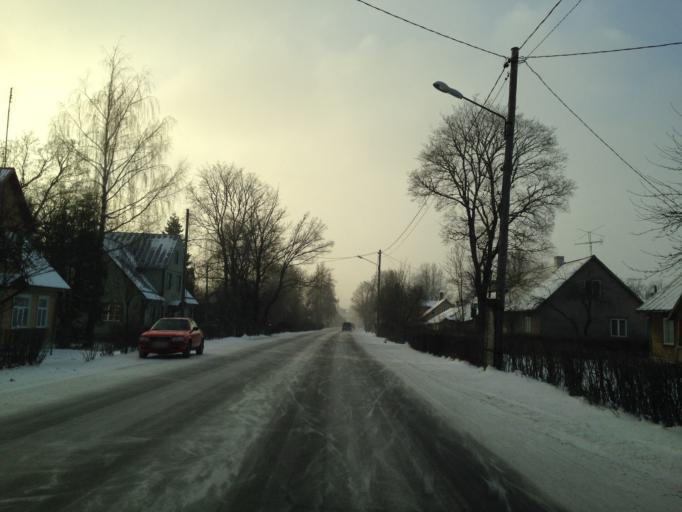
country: EE
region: Raplamaa
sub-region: Maerjamaa vald
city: Marjamaa
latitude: 58.9078
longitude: 24.4312
